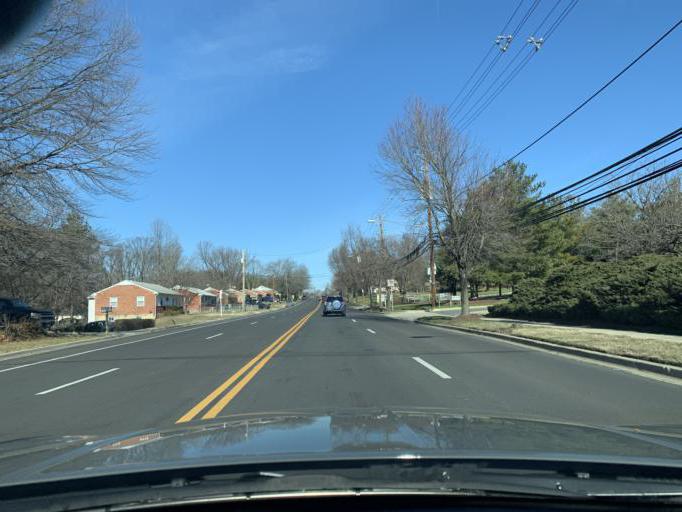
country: US
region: Maryland
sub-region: Prince George's County
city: Largo
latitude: 38.8936
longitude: -76.8510
